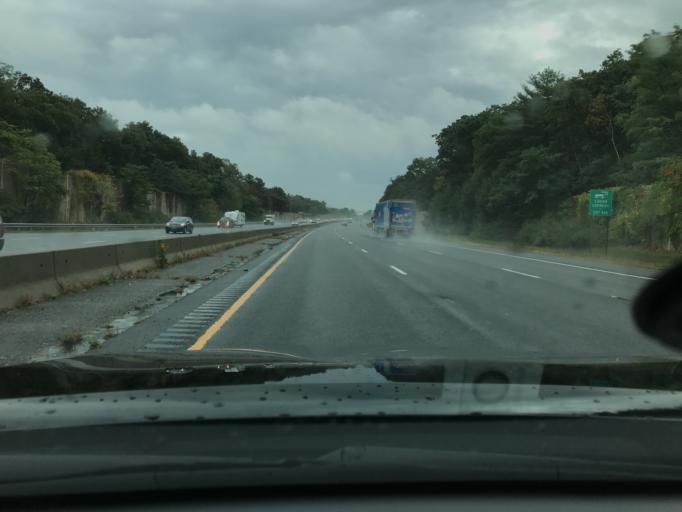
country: US
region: Massachusetts
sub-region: Essex County
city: Lynnfield
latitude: 42.5160
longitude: -71.0114
